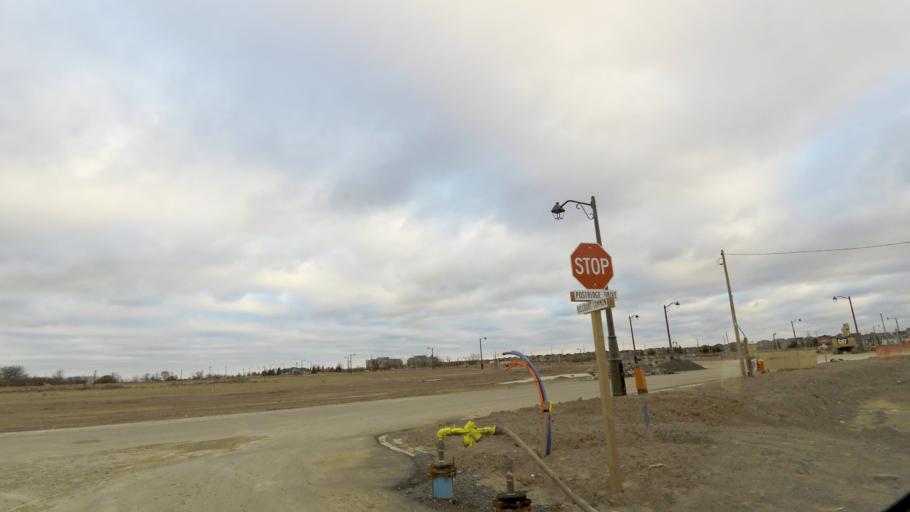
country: CA
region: Ontario
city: Oakville
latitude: 43.4929
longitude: -79.7205
